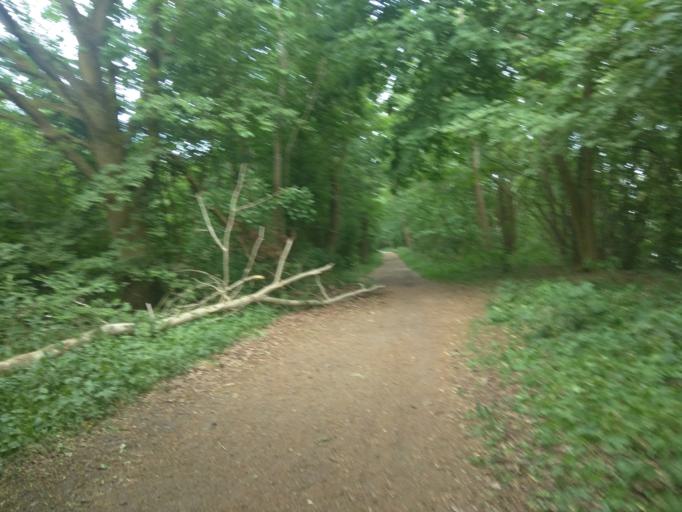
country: DE
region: Schleswig-Holstein
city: Kruzen
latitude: 53.3730
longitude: 10.5285
